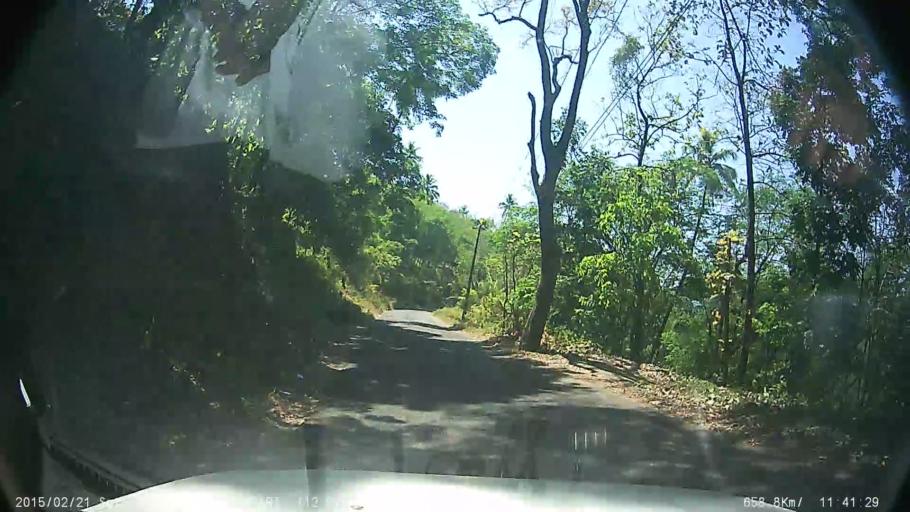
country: IN
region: Kerala
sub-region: Kottayam
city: Lalam
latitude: 9.7944
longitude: 76.7283
